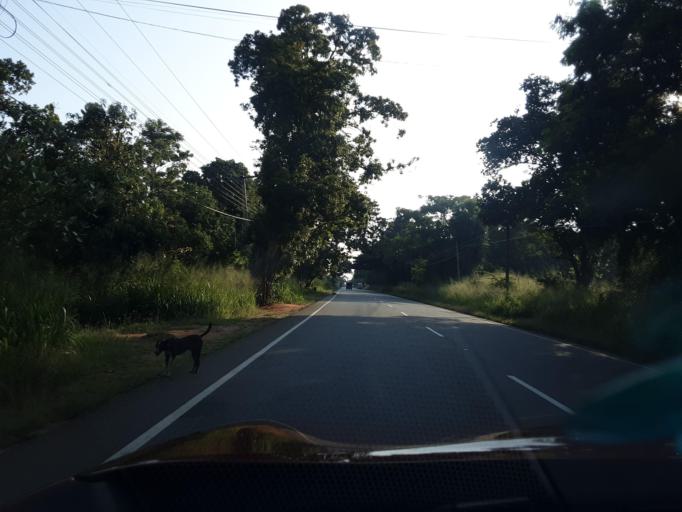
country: LK
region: Central
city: Sigiriya
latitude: 7.9880
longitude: 80.7227
